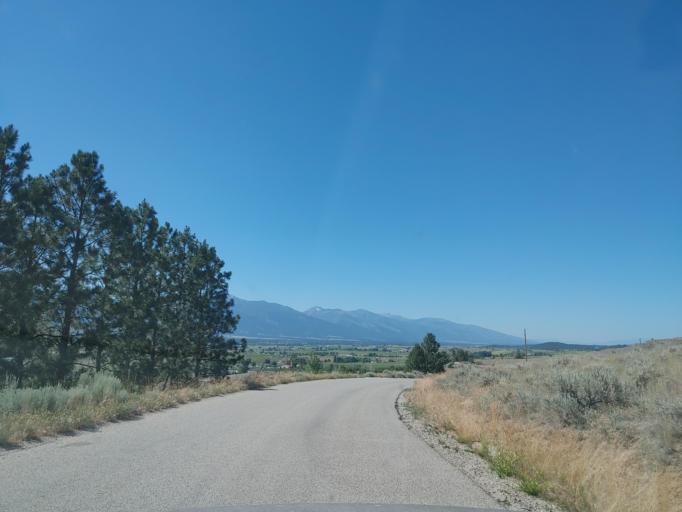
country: US
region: Montana
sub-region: Ravalli County
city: Hamilton
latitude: 46.3475
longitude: -114.0519
